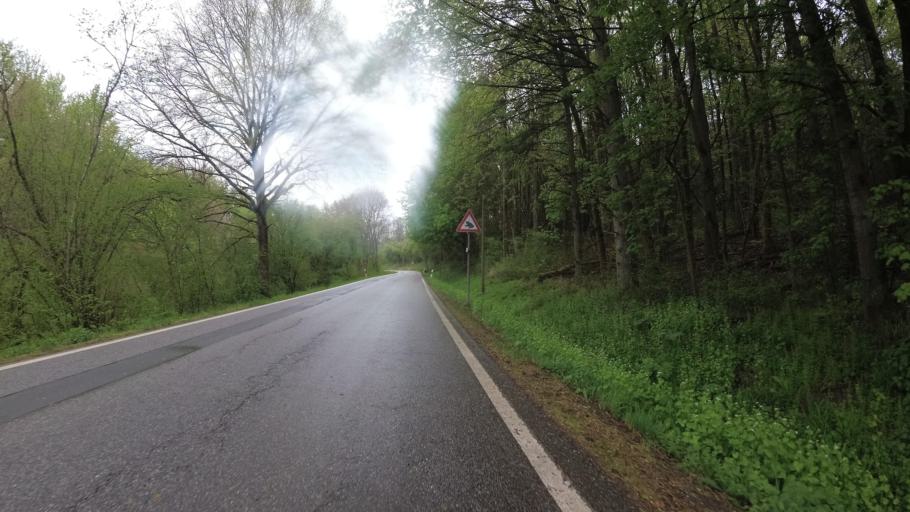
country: FR
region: Lorraine
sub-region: Departement de la Moselle
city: Bouzonville
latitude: 49.3298
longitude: 6.6061
